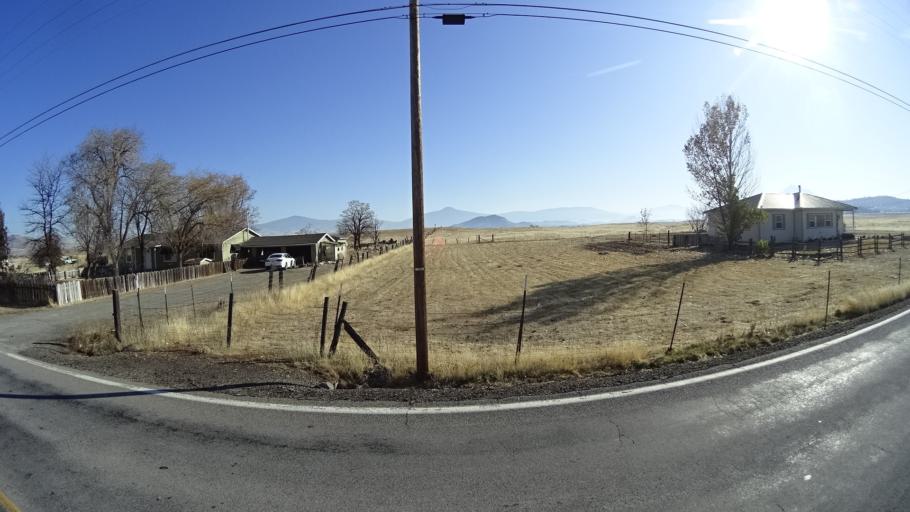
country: US
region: California
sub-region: Siskiyou County
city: Yreka
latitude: 41.7203
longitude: -122.5933
